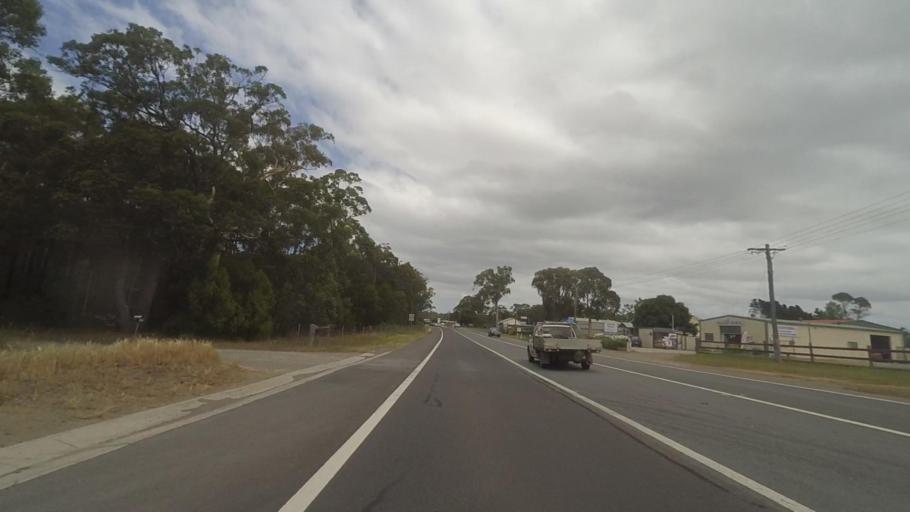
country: AU
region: New South Wales
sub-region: Shoalhaven Shire
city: Falls Creek
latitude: -35.0892
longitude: 150.5100
